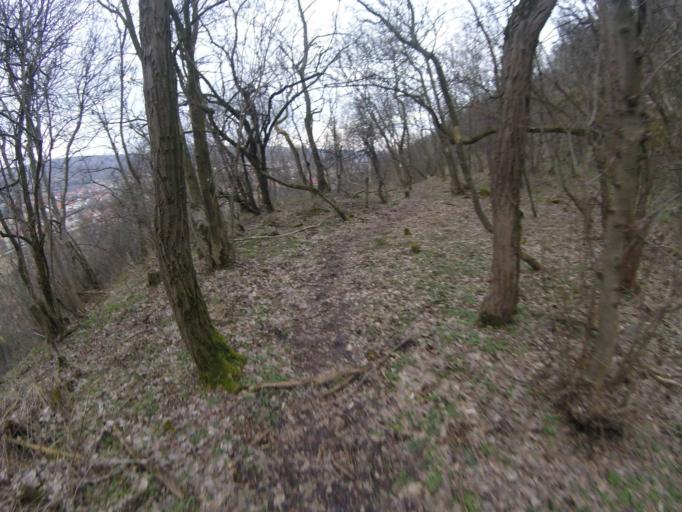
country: HU
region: Heves
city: Kerecsend
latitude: 47.8308
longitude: 20.3361
